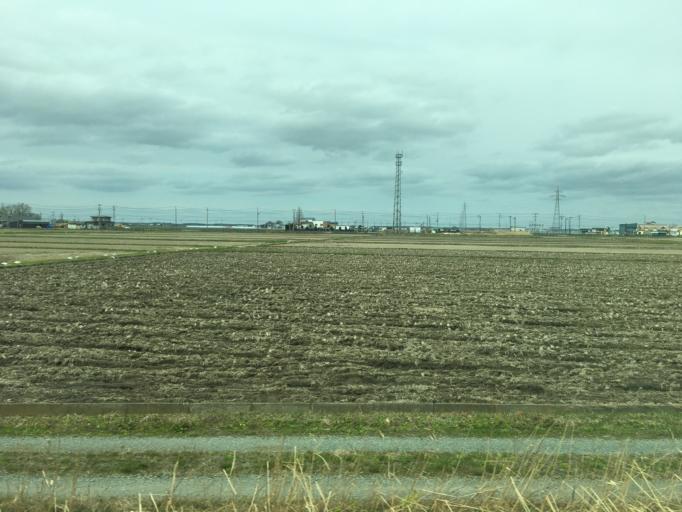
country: JP
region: Aomori
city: Shimokizukuri
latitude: 40.7999
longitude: 140.3820
